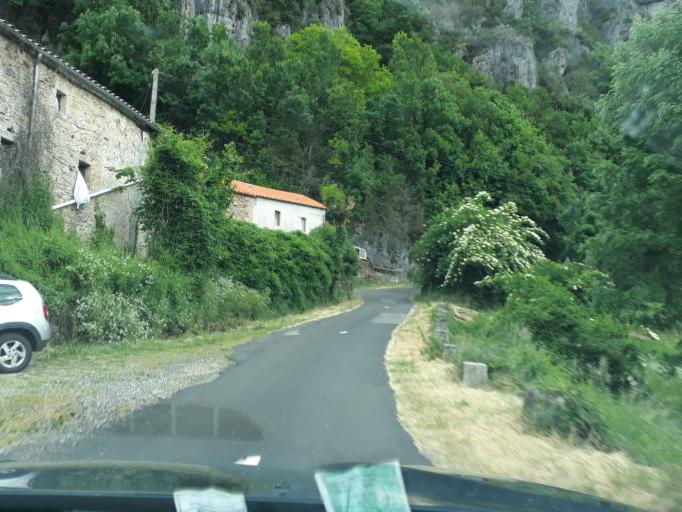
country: FR
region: Languedoc-Roussillon
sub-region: Departement de l'Herault
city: Lodeve
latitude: 43.8033
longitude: 3.2656
